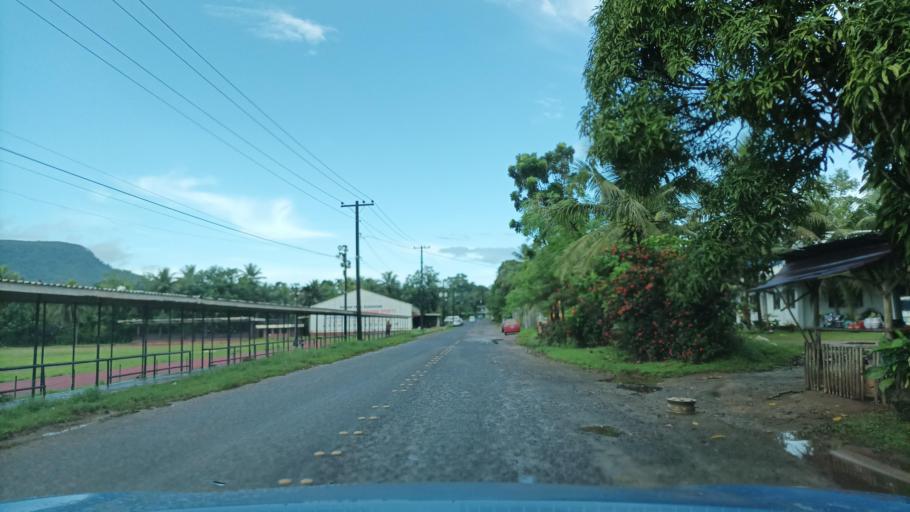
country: FM
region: Pohnpei
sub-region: Kolonia Municipality
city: Kolonia Town
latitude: 6.9508
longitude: 158.2050
